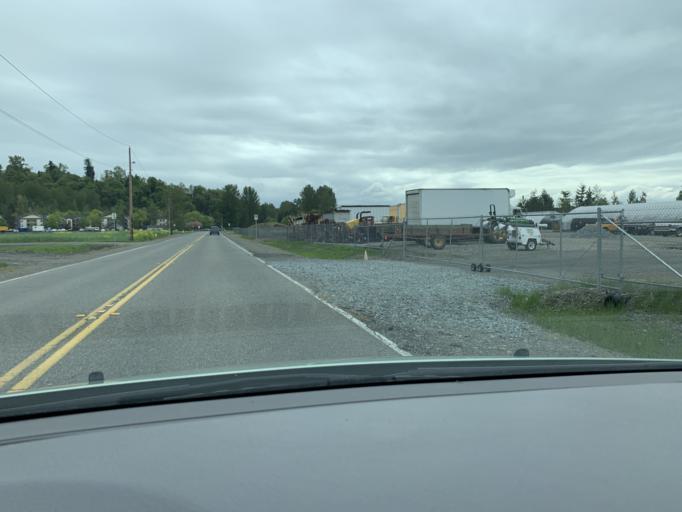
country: US
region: Washington
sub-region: King County
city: Kent
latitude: 47.3969
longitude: -122.2233
